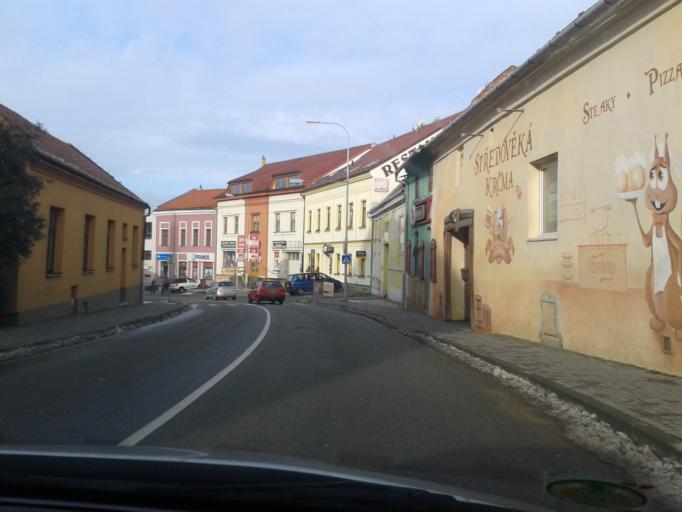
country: CZ
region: South Moravian
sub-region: Okres Blansko
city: Boskovice
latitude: 49.4872
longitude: 16.6622
